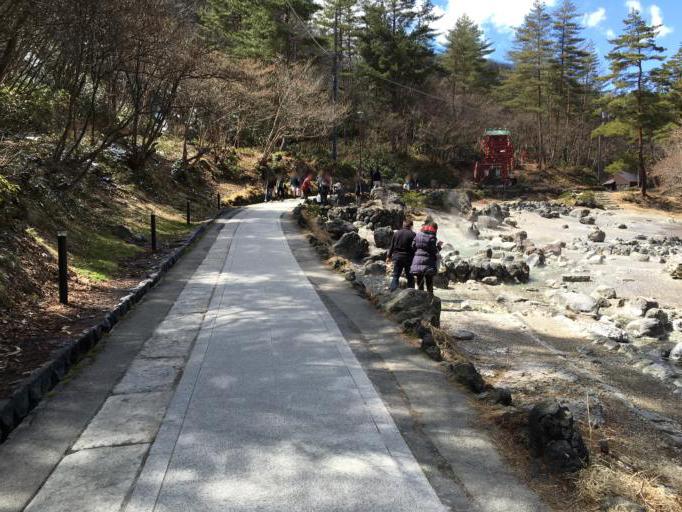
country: JP
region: Gunma
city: Nakanojomachi
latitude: 36.6239
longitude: 138.5916
